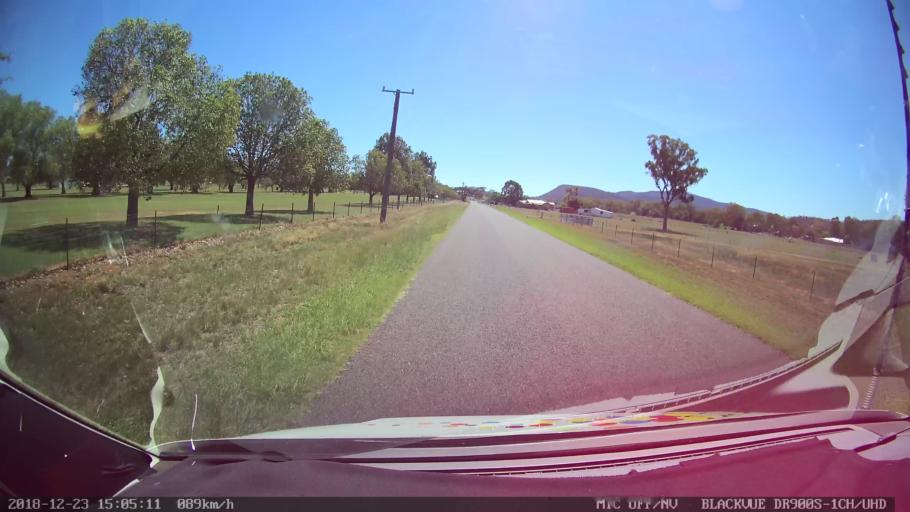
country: AU
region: New South Wales
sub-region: Tamworth Municipality
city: Manilla
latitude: -30.7427
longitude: 150.7418
